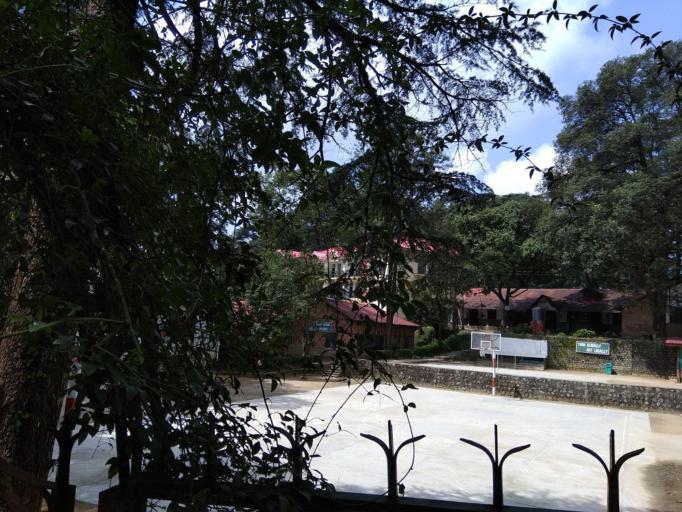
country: IN
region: Himachal Pradesh
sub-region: Kangra
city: Palampur
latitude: 32.1146
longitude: 76.5382
